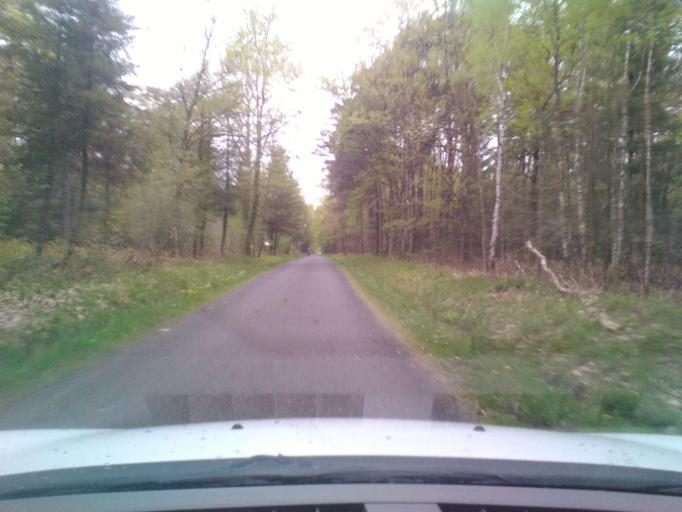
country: FR
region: Rhone-Alpes
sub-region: Departement de l'Ain
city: Saint-Etienne-du-Bois
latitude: 46.2561
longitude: 5.2852
